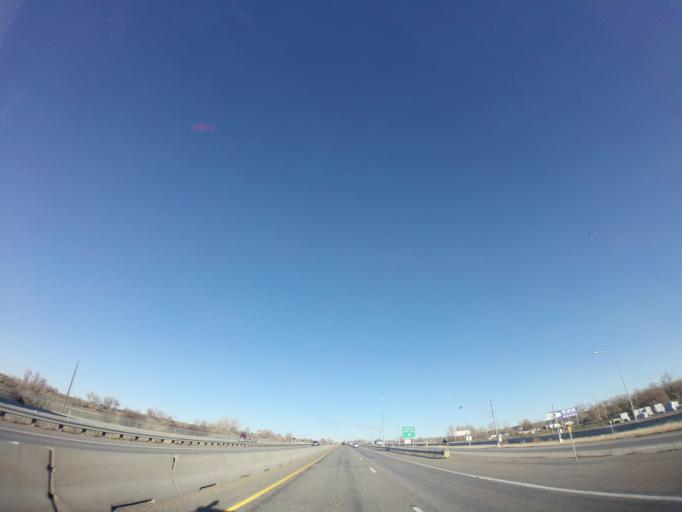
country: US
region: Montana
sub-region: Yellowstone County
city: Laurel
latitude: 45.6914
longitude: -108.6869
